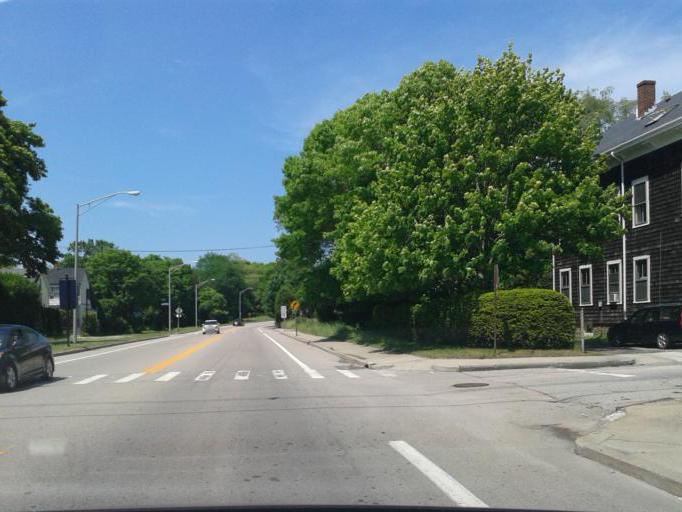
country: US
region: Rhode Island
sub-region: Newport County
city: Newport
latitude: 41.4927
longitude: -71.3174
